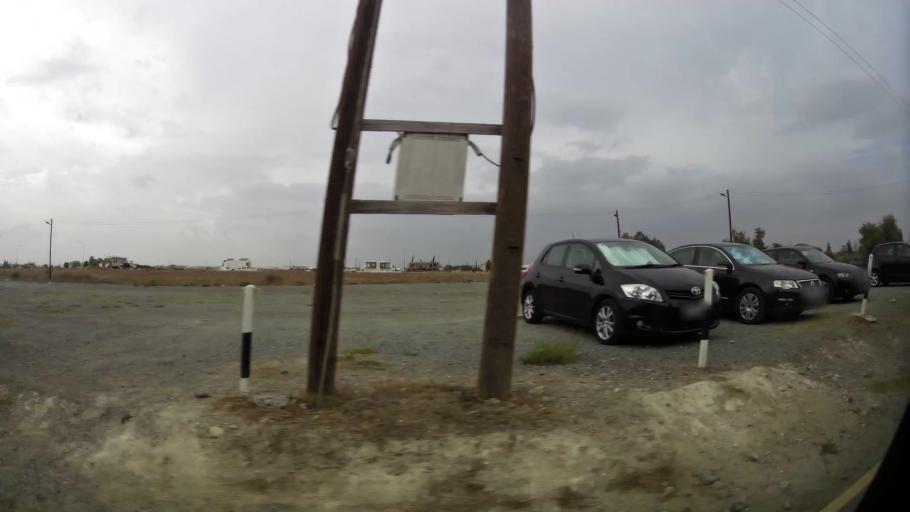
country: CY
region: Lefkosia
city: Geri
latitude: 35.0897
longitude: 33.3933
